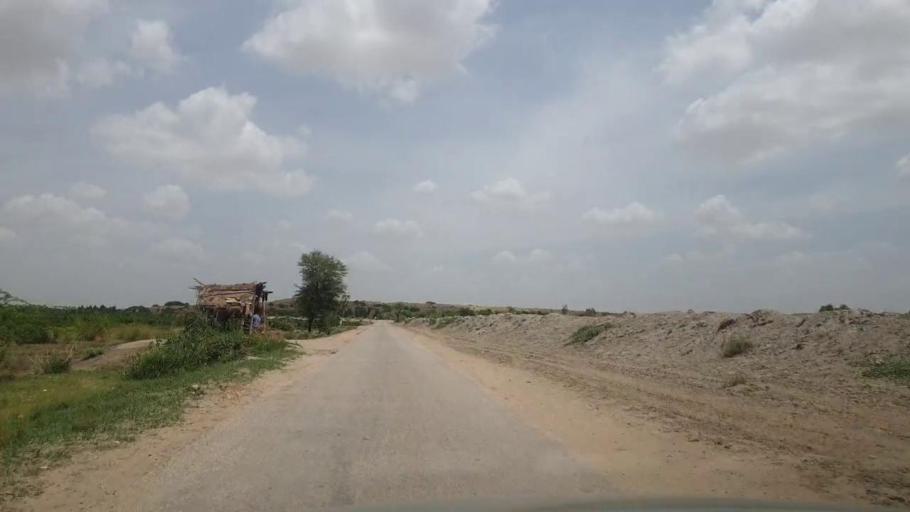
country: PK
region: Sindh
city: Kot Diji
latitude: 27.1995
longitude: 69.0633
